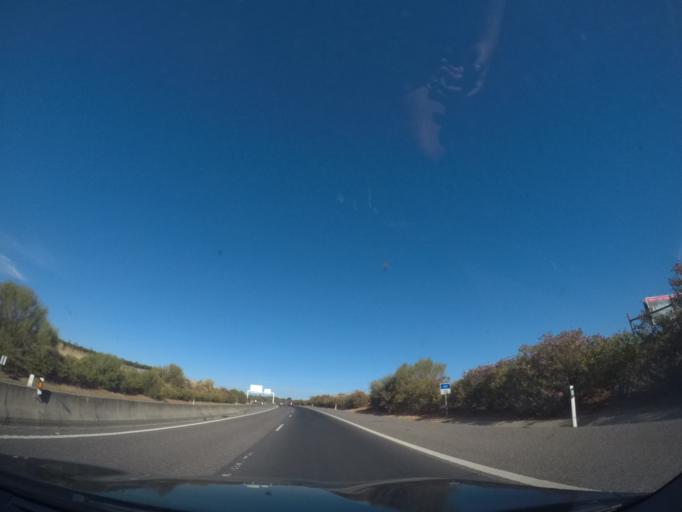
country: PT
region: Faro
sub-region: Silves
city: Armacao de Pera
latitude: 37.1398
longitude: -8.3696
